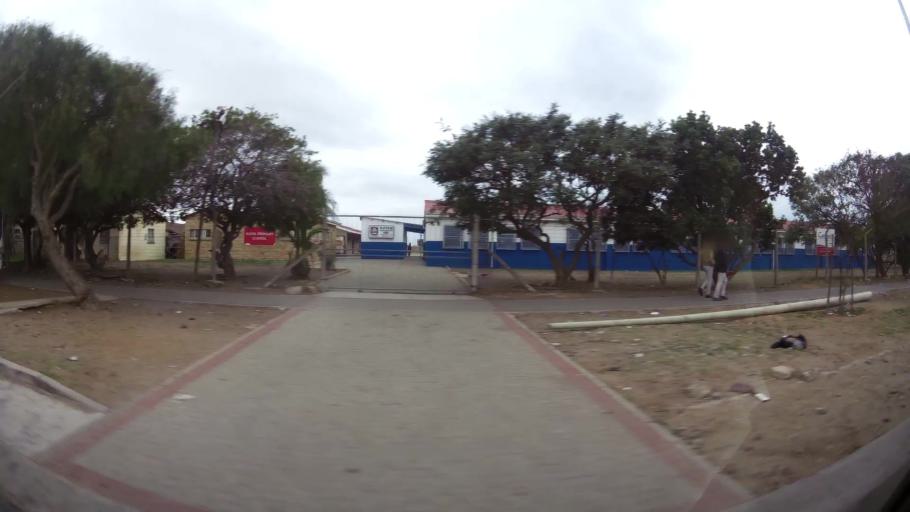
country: ZA
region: Eastern Cape
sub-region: Nelson Mandela Bay Metropolitan Municipality
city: Port Elizabeth
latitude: -33.9042
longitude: 25.5986
